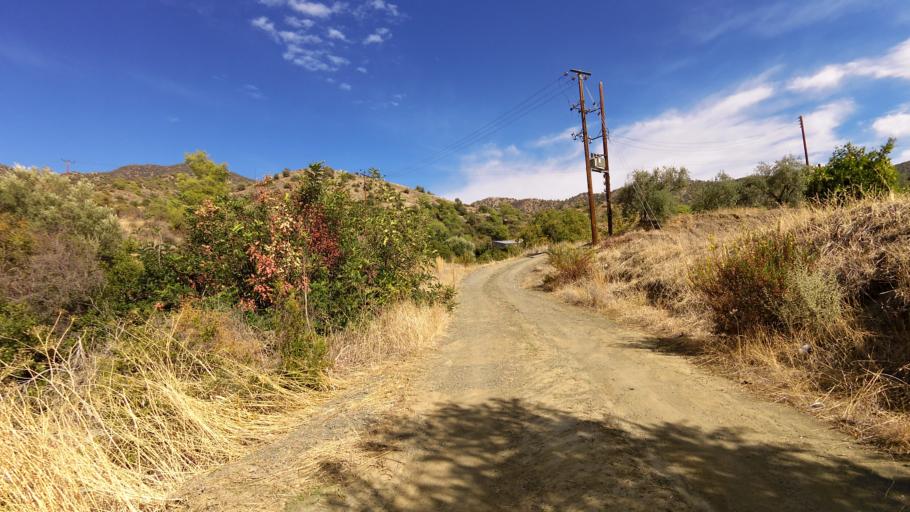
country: CY
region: Limassol
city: Mouttagiaka
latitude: 34.7777
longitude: 33.0727
